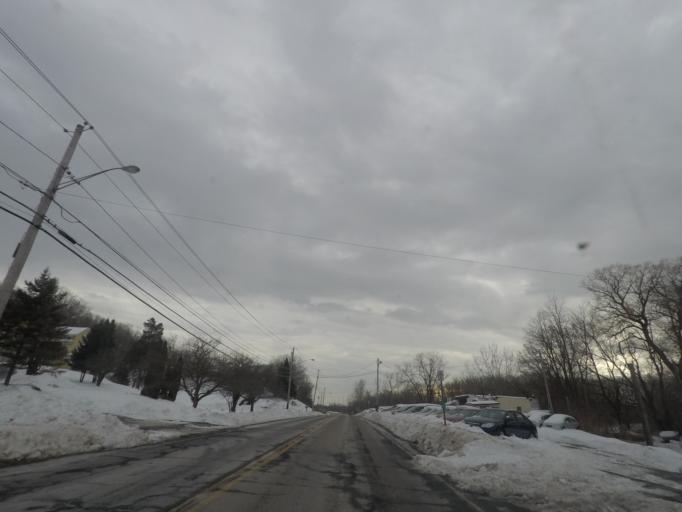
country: US
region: New York
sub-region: Rensselaer County
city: Hampton Manor
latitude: 42.6198
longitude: -73.7457
